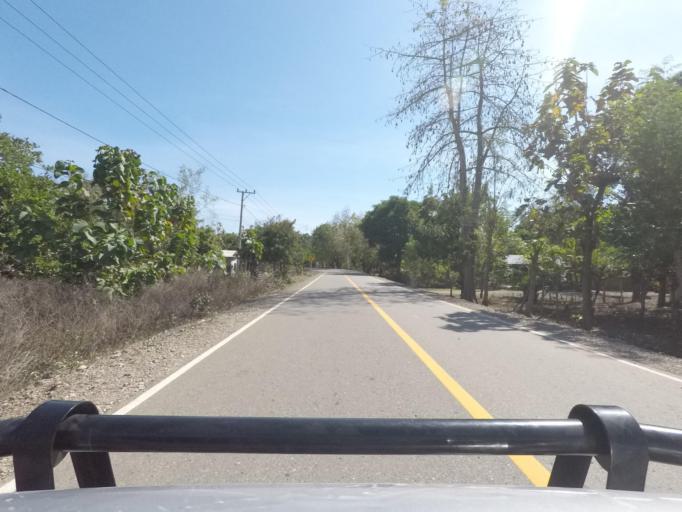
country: TL
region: Bobonaro
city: Maliana
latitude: -8.8947
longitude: 125.0061
